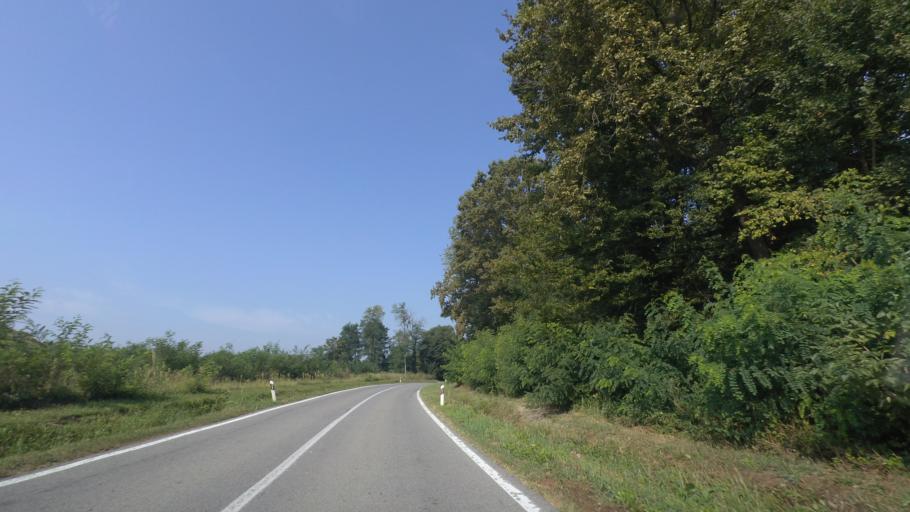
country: HR
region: Sisacko-Moslavacka
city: Novska
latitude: 45.3630
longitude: 16.9788
